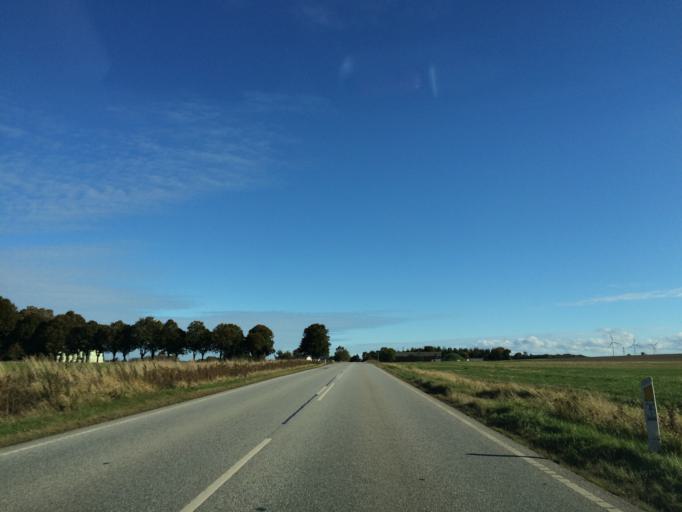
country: DK
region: Central Jutland
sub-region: Randers Kommune
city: Randers
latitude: 56.3987
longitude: 9.9870
